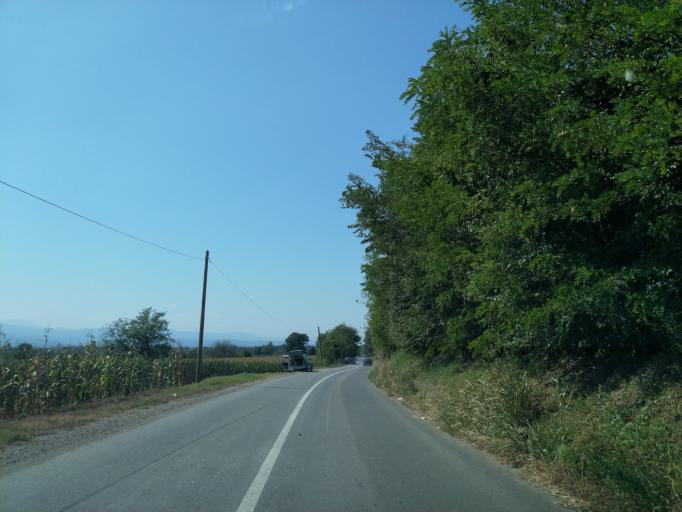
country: RS
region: Central Serbia
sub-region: Rasinski Okrug
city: Krusevac
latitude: 43.6195
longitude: 21.1718
